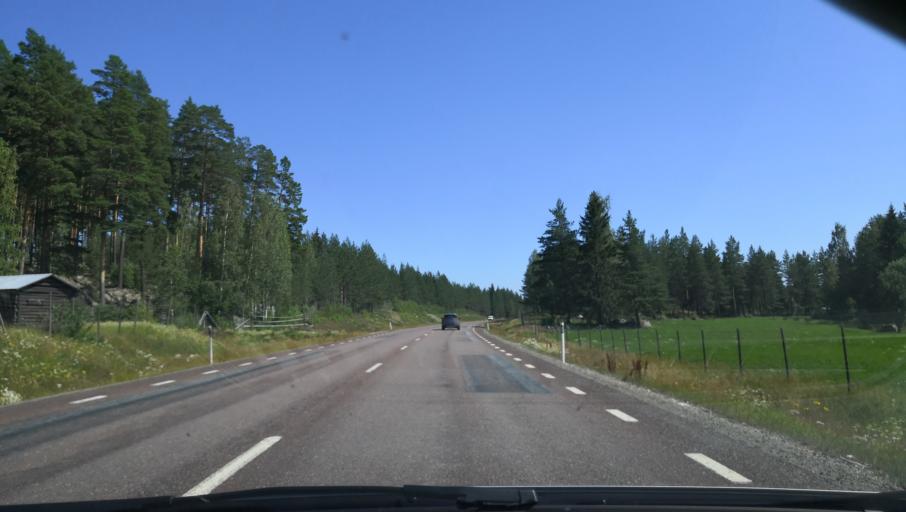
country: SE
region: Gaevleborg
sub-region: Ovanakers Kommun
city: Alfta
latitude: 61.3429
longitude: 16.1257
